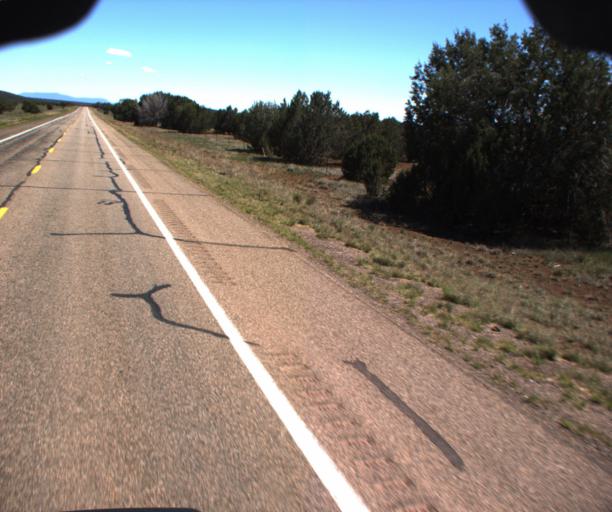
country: US
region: Arizona
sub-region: Yavapai County
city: Paulden
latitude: 35.1580
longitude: -112.4544
